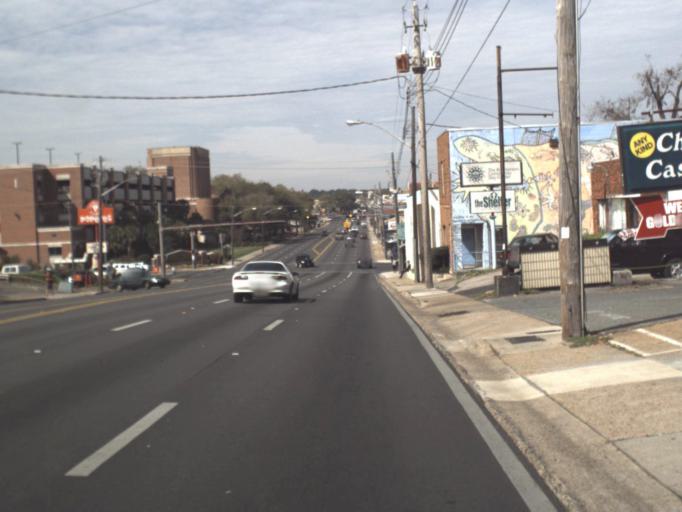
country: US
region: Florida
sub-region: Leon County
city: Tallahassee
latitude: 30.4448
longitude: -84.2872
